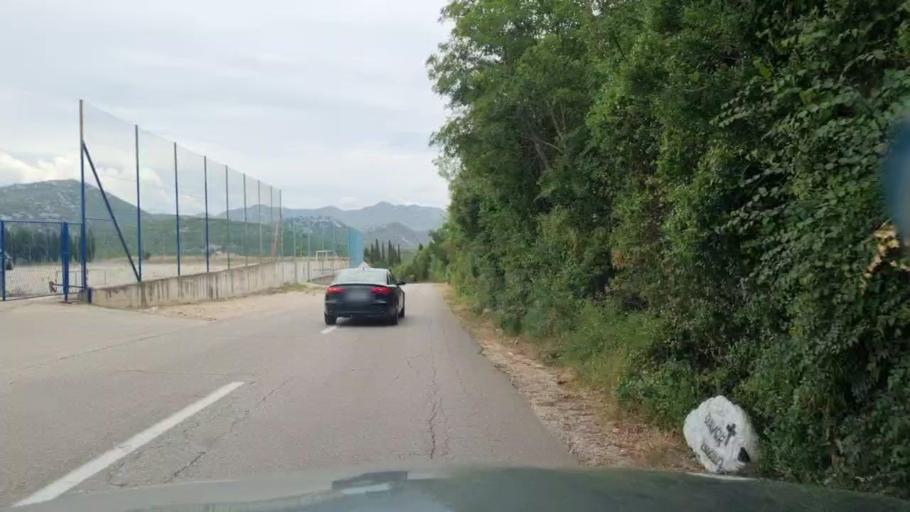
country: BA
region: Federation of Bosnia and Herzegovina
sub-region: Hercegovacko-Bosanski Kanton
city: Neum
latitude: 42.9231
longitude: 17.6374
